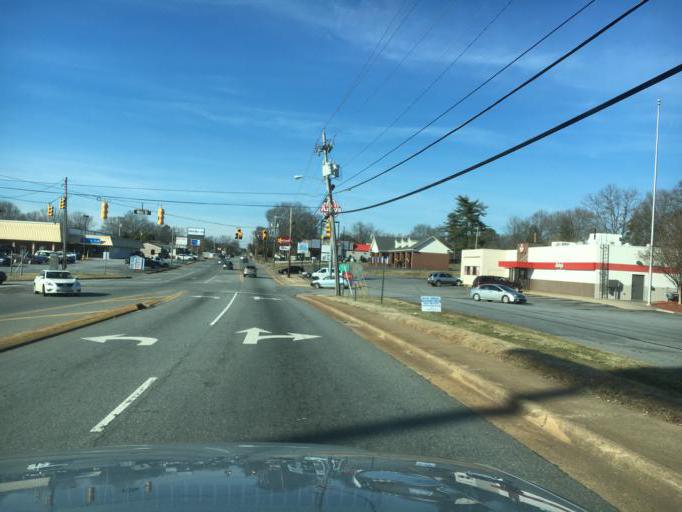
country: US
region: North Carolina
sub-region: Rutherford County
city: Forest City
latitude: 35.3169
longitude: -81.8574
